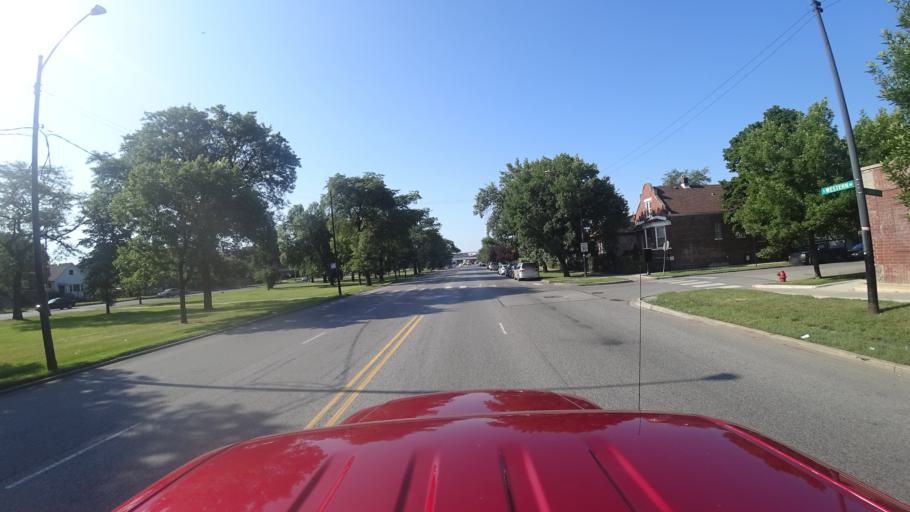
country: US
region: Illinois
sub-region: Cook County
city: Chicago
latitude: 41.8078
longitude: -87.6845
